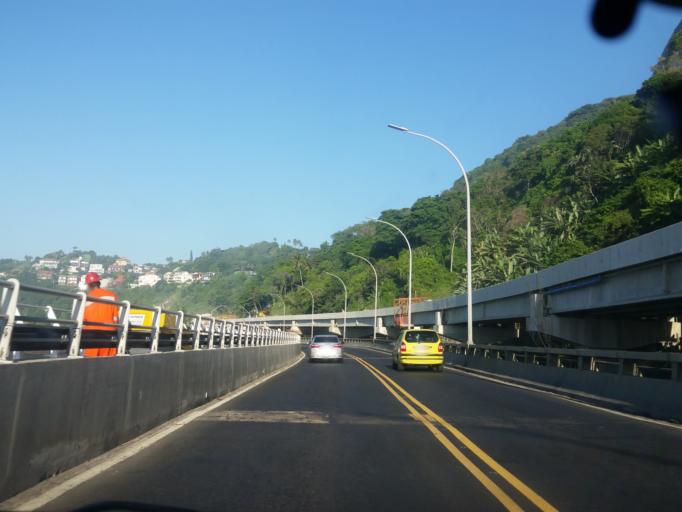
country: BR
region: Rio de Janeiro
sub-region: Rio De Janeiro
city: Rio de Janeiro
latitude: -23.0059
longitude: -43.2807
